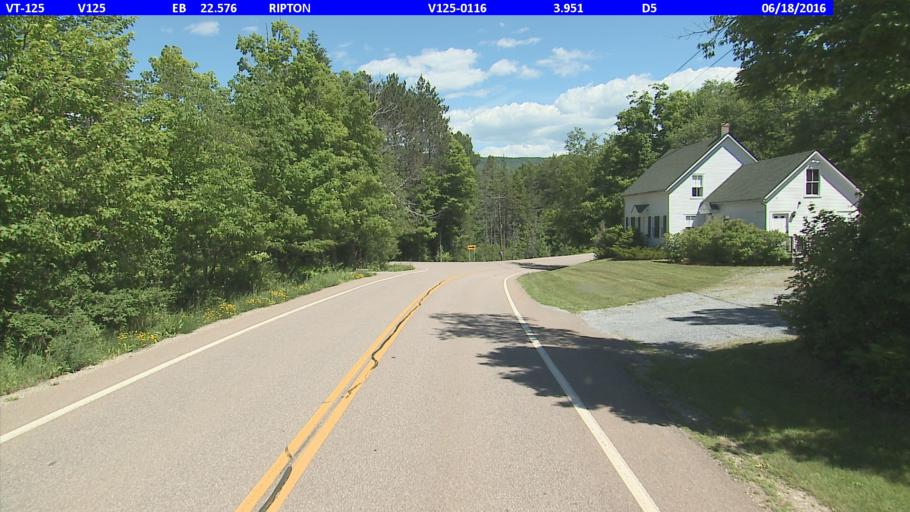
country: US
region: Vermont
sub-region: Rutland County
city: Brandon
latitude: 43.9560
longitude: -72.9975
